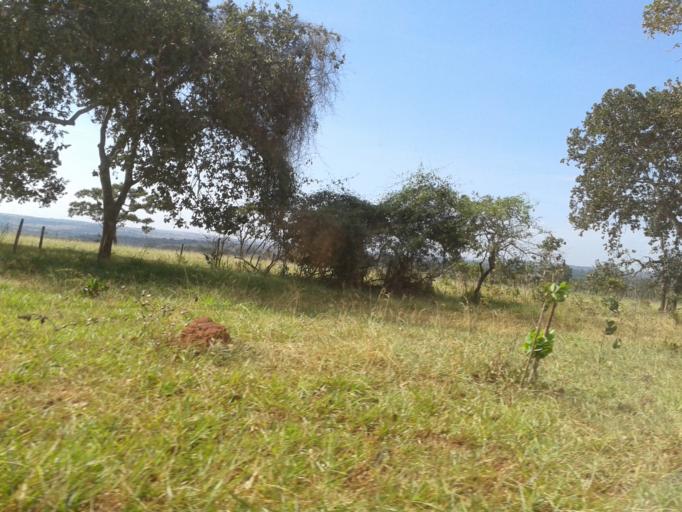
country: BR
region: Minas Gerais
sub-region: Ituiutaba
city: Ituiutaba
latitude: -19.0620
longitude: -49.3642
